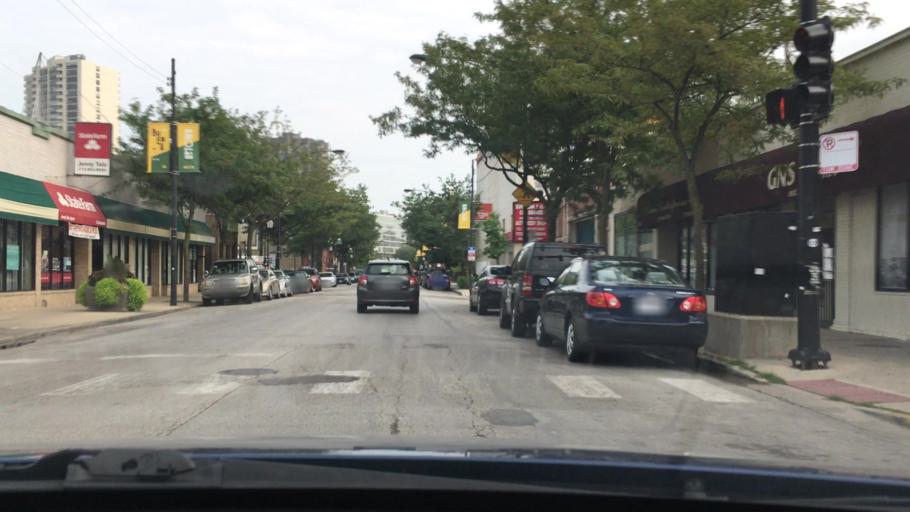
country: US
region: Illinois
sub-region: Cook County
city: Lincolnwood
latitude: 41.9569
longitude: -87.6521
